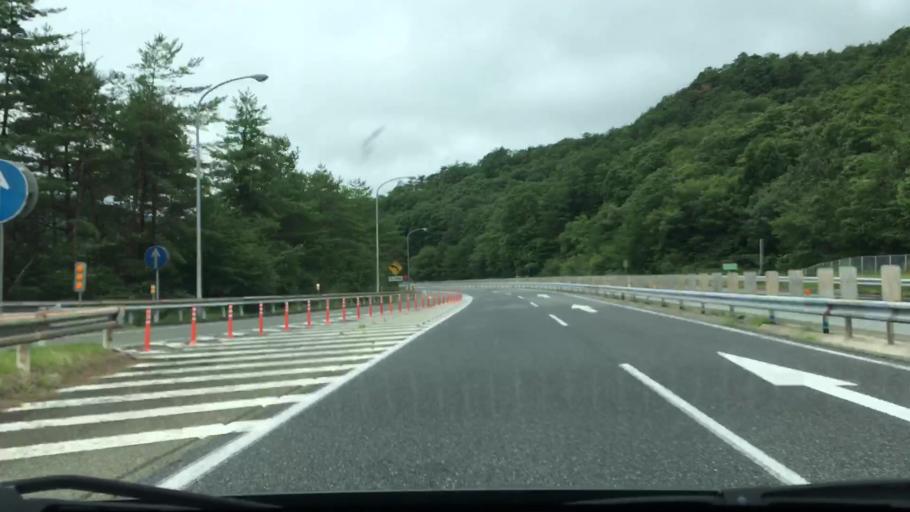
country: JP
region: Hiroshima
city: Shobara
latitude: 34.8615
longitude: 133.1031
